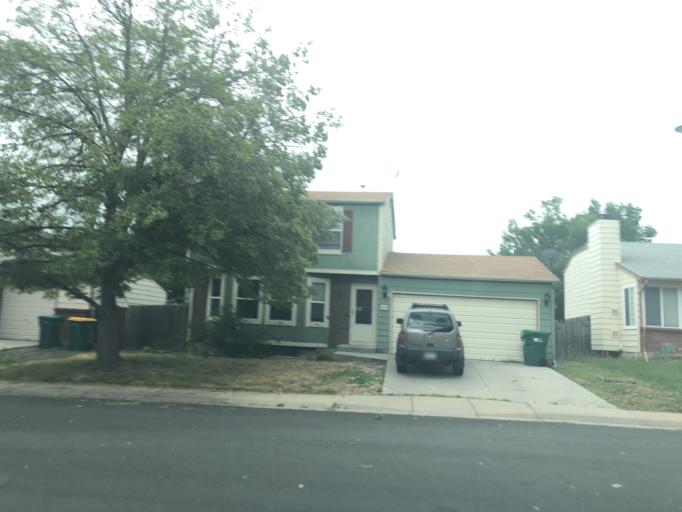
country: US
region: Colorado
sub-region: Arapahoe County
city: Dove Valley
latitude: 39.6281
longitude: -104.7877
